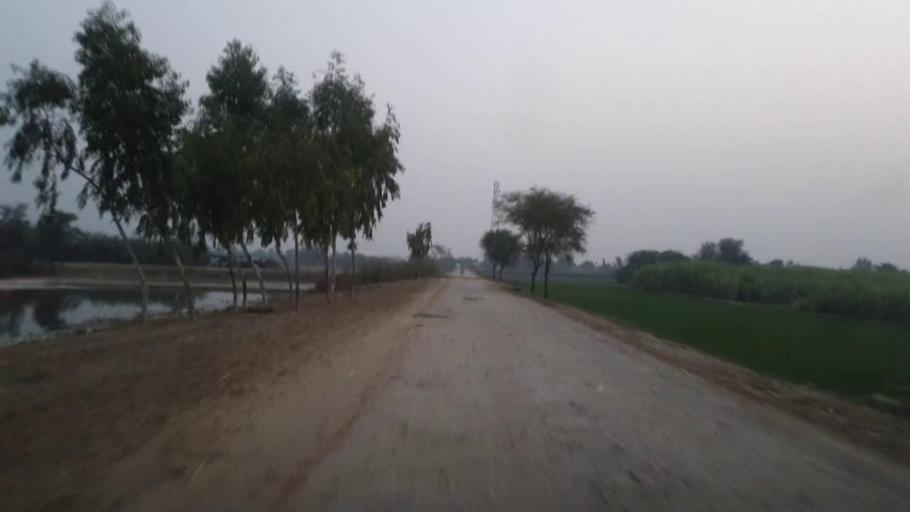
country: PK
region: Sindh
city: Karaundi
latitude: 26.9253
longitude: 68.4299
